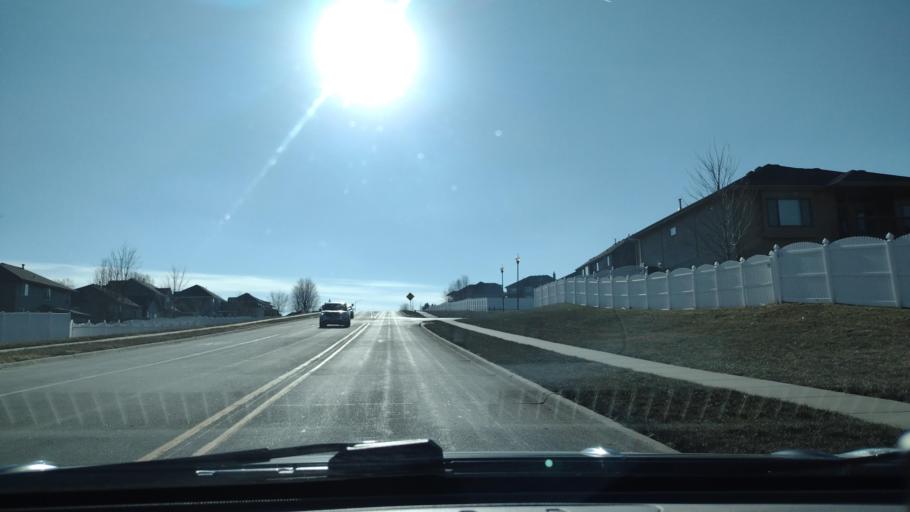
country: US
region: Nebraska
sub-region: Sarpy County
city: La Vista
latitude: 41.1647
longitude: -96.0142
